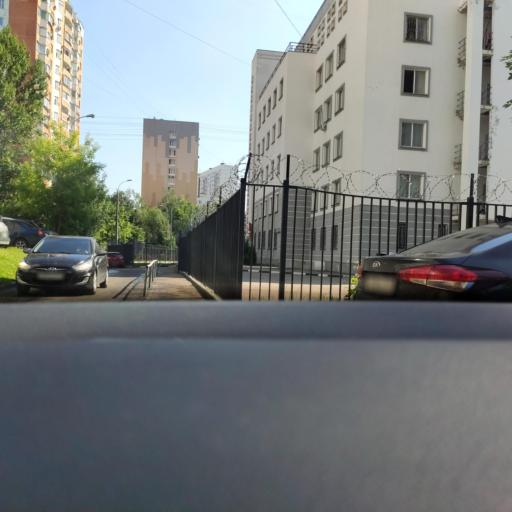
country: RU
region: Moscow
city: Vatutino
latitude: 55.8901
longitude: 37.6552
